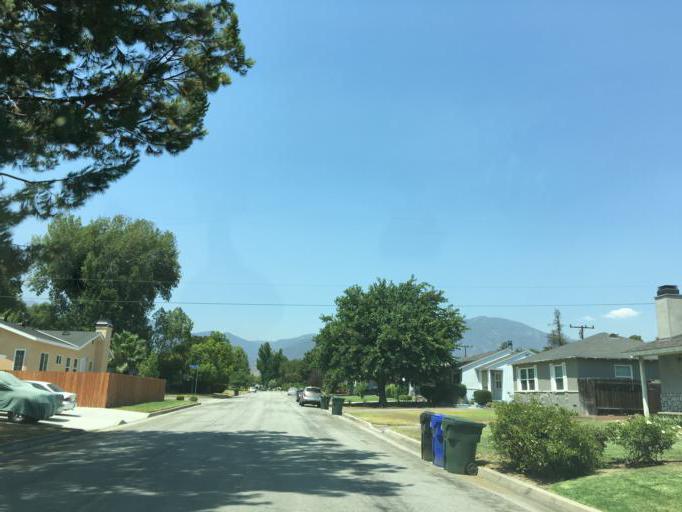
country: US
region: California
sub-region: Los Angeles County
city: Mayflower Village
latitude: 34.1152
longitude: -118.0135
